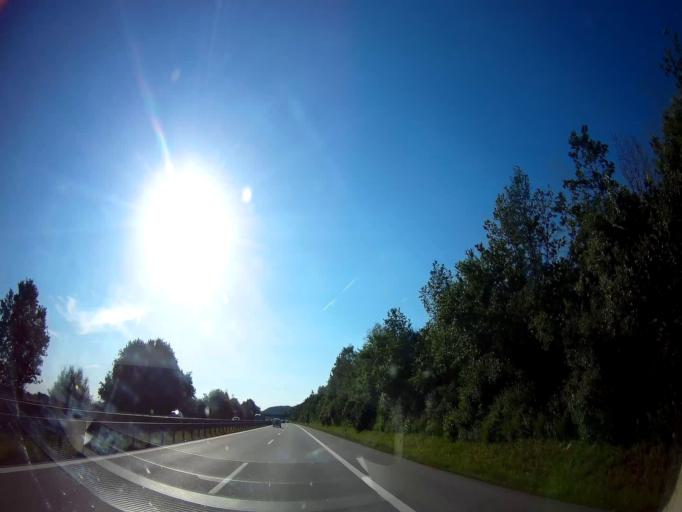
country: DE
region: Bavaria
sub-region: Lower Bavaria
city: Aholfing
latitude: 48.9834
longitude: 12.4598
